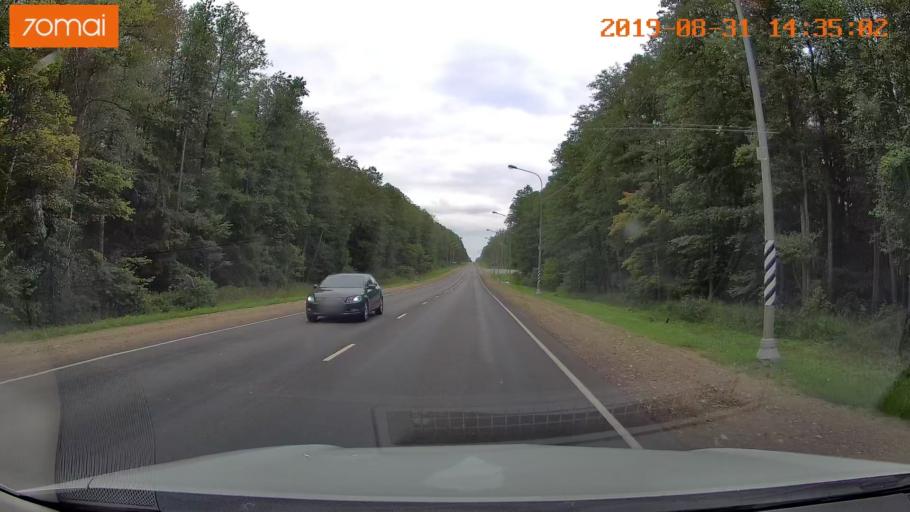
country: RU
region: Smolensk
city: Yekimovichi
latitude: 54.1605
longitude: 33.4479
